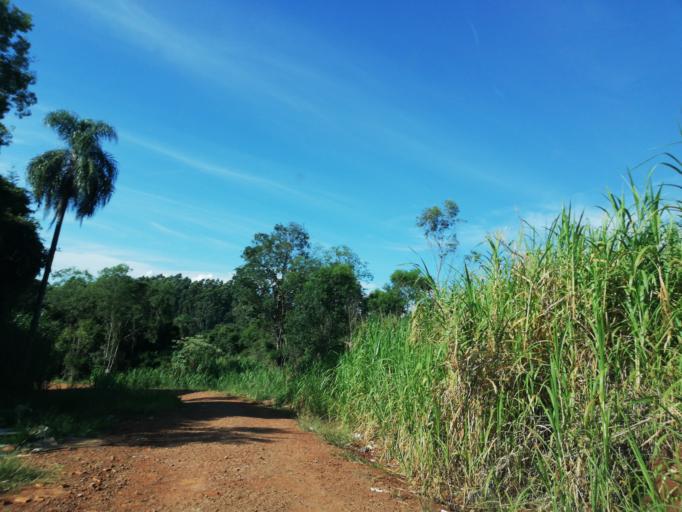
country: AR
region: Misiones
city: Dos de Mayo
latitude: -26.9902
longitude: -54.4955
